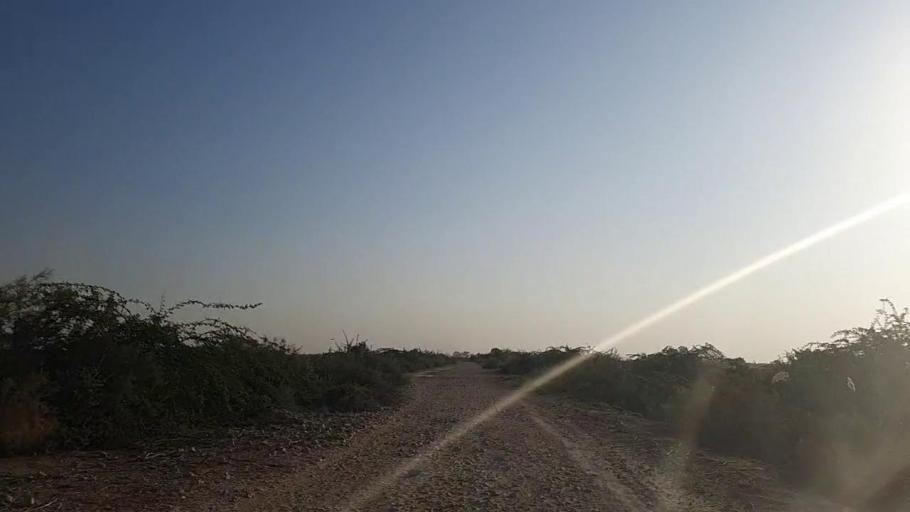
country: PK
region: Sindh
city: Jati
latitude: 24.4388
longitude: 68.1932
